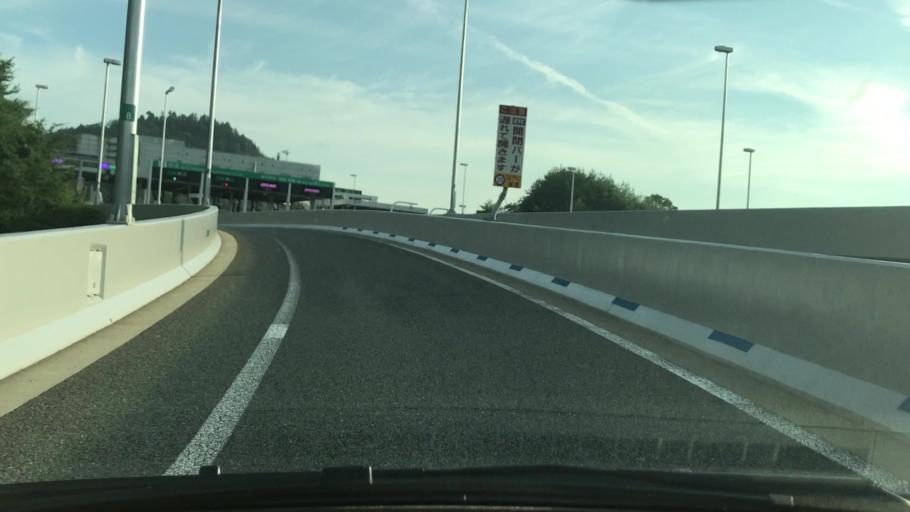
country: JP
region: Hyogo
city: Sandacho
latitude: 34.8327
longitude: 135.2589
